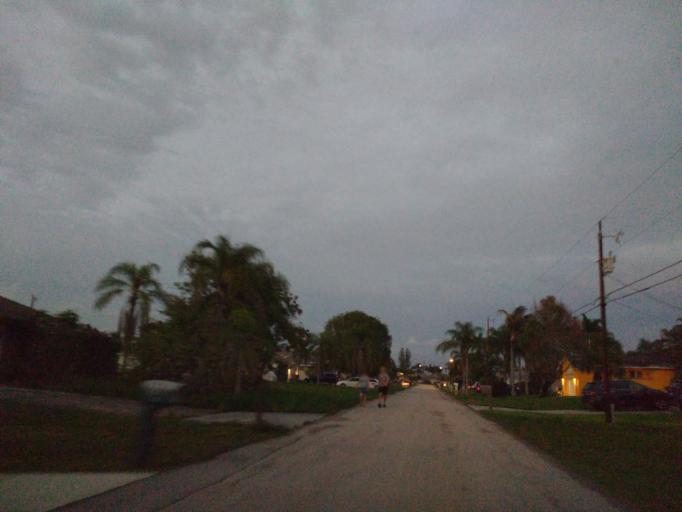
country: US
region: Florida
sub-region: Lee County
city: Cape Coral
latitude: 26.6151
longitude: -81.9661
